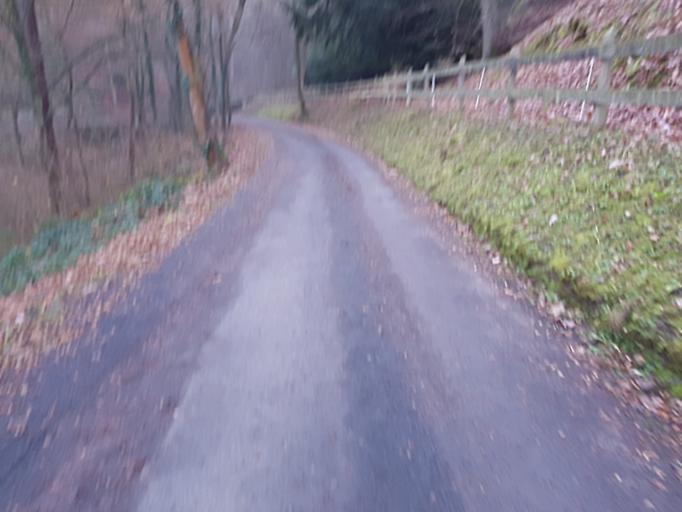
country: DE
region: Bavaria
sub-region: Regierungsbezirk Unterfranken
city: Miltenberg
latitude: 49.6982
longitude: 9.2509
